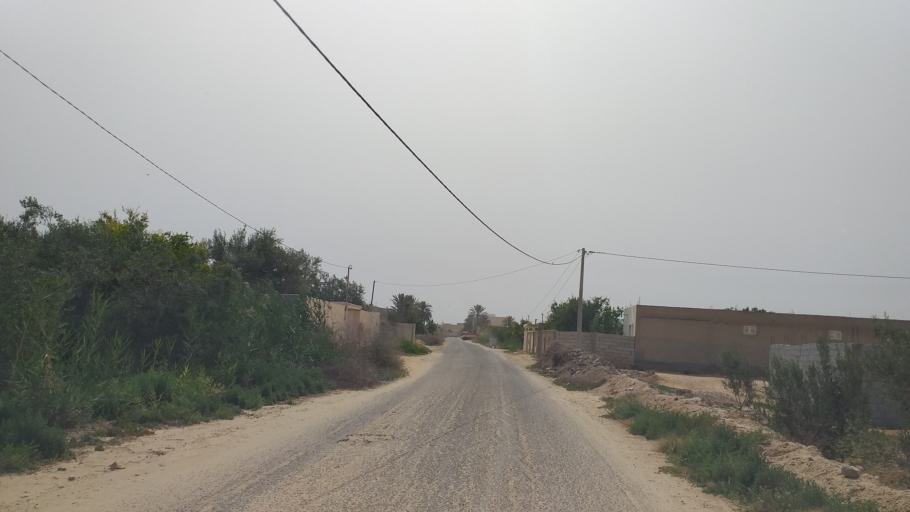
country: TN
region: Qabis
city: Gabes
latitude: 33.9453
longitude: 10.0523
